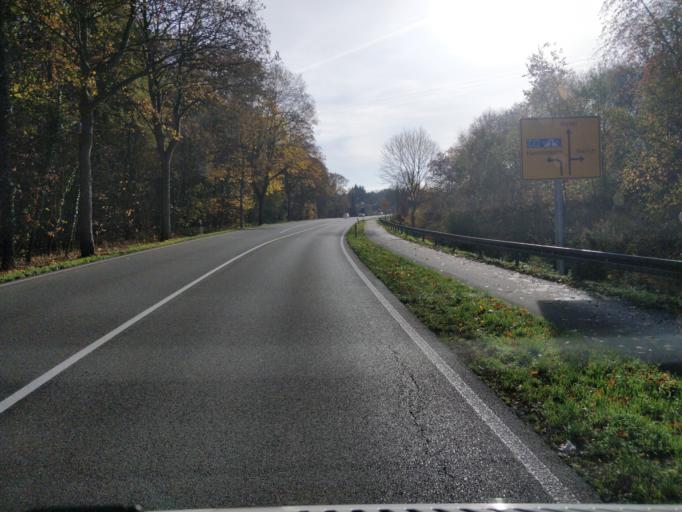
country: DE
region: North Rhine-Westphalia
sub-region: Regierungsbezirk Dusseldorf
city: Mehrhoog
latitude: 51.7192
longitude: 6.5138
